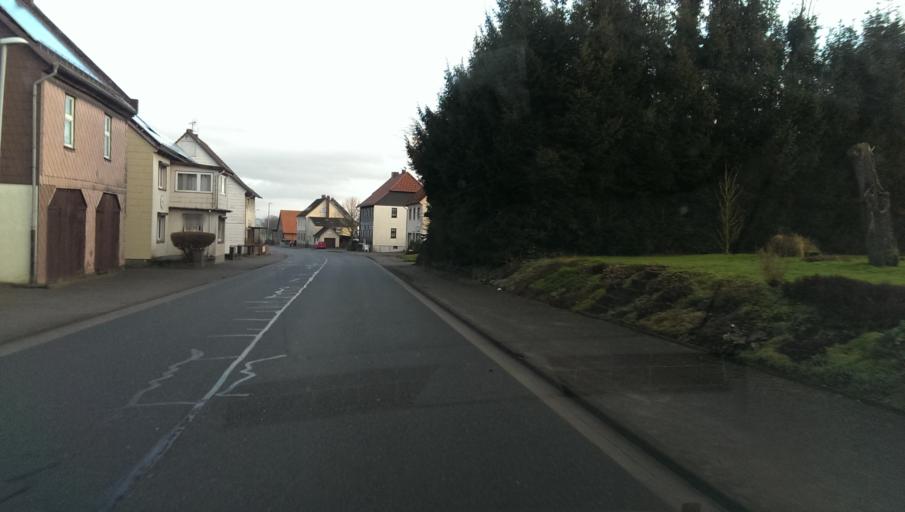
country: DE
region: Lower Saxony
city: Eimen
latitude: 51.8865
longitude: 9.7499
